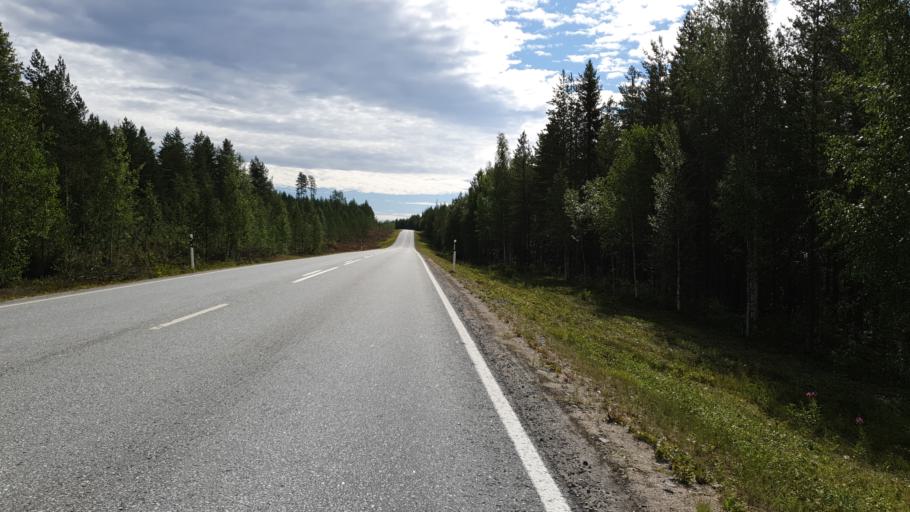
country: FI
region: Kainuu
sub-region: Kehys-Kainuu
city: Kuhmo
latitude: 64.4909
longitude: 29.8450
